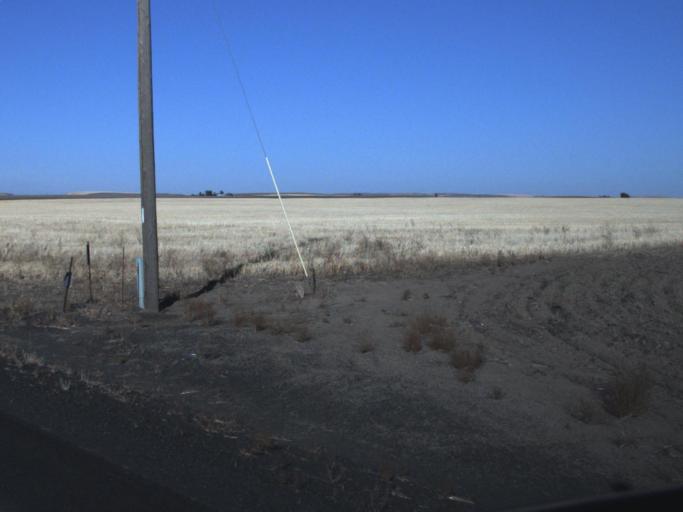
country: US
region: Washington
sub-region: Adams County
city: Ritzville
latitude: 46.9427
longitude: -118.3434
